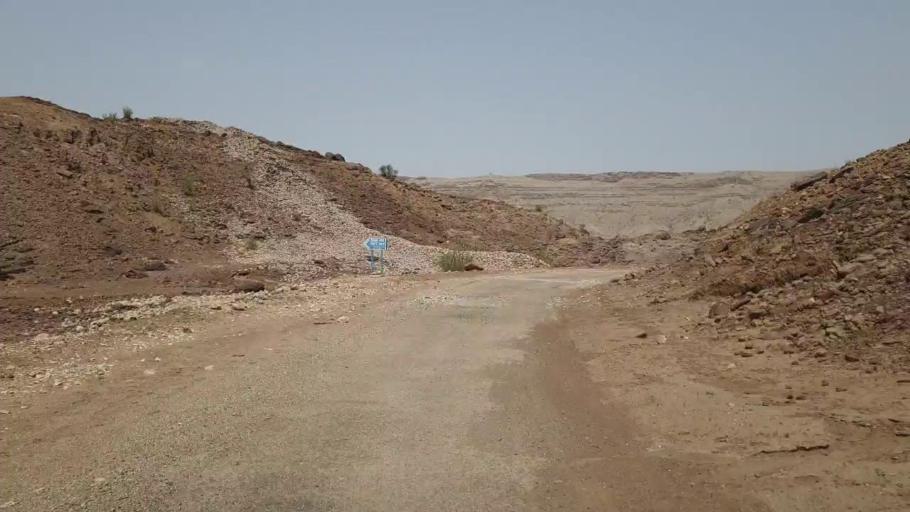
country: PK
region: Sindh
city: Sann
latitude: 25.8841
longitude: 67.9023
